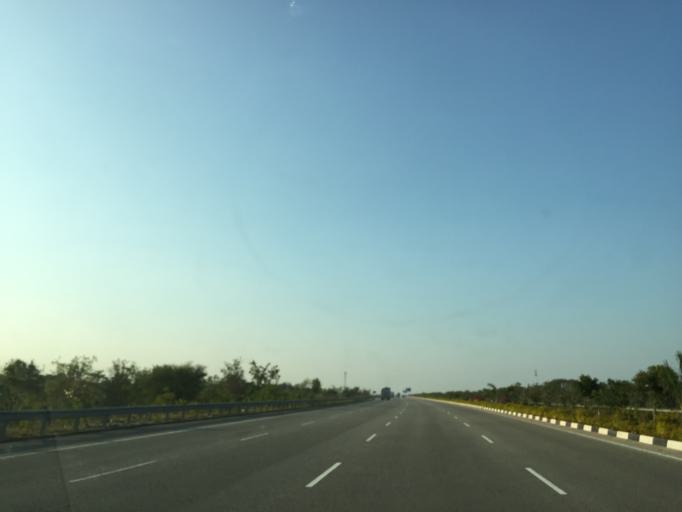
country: IN
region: Telangana
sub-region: Rangareddi
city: Ghatkesar
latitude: 17.5052
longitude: 78.6547
